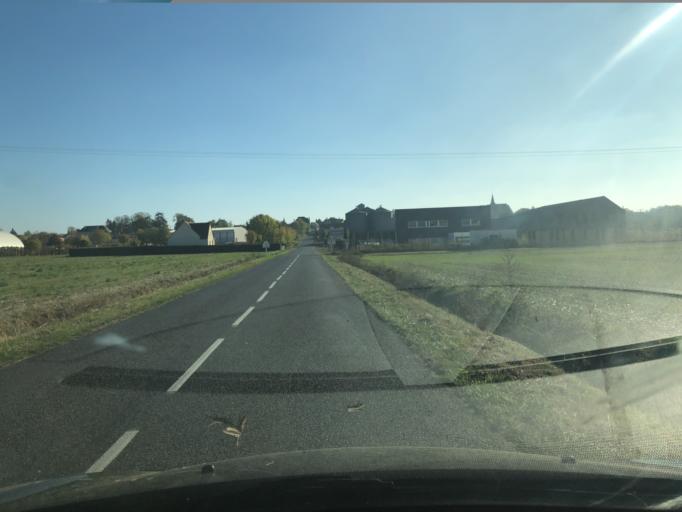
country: FR
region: Centre
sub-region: Departement d'Indre-et-Loire
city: Neuvy-le-Roi
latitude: 47.6094
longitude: 0.5965
